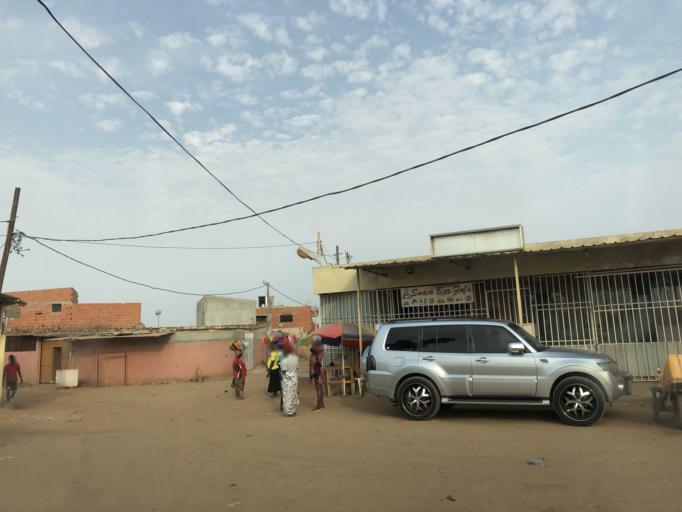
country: AO
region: Luanda
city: Luanda
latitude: -8.9118
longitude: 13.1724
